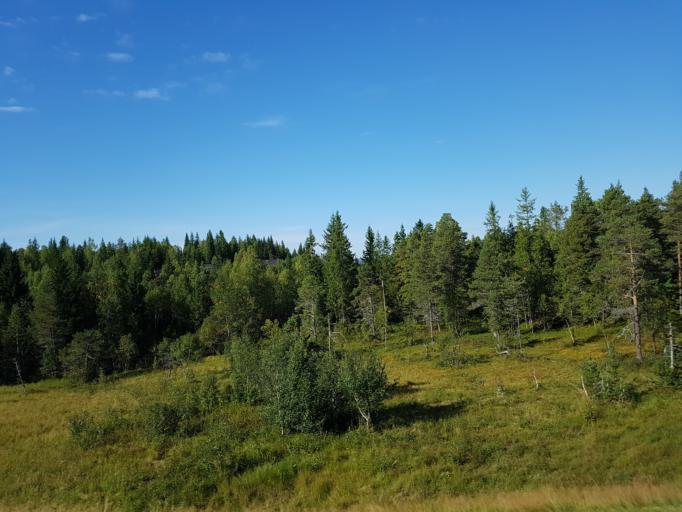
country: NO
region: Sor-Trondelag
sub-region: Trondheim
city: Trondheim
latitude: 63.6438
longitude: 10.2696
